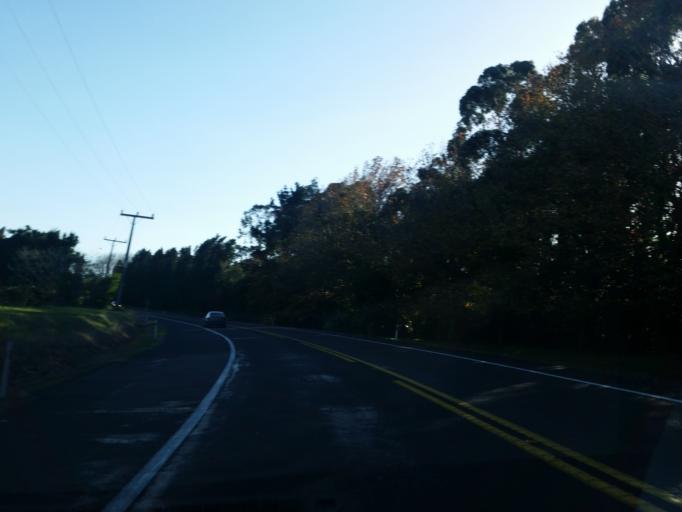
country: NZ
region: Bay of Plenty
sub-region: Western Bay of Plenty District
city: Katikati
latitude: -37.5226
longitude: 175.9201
